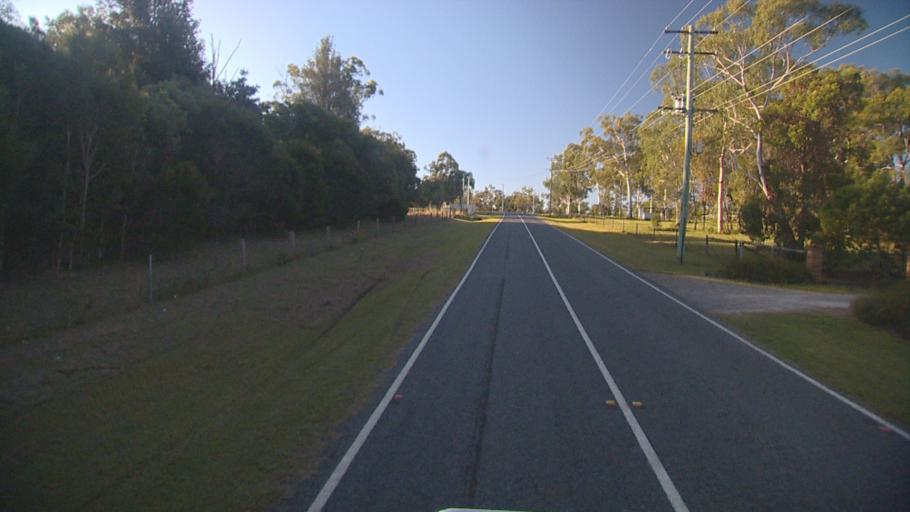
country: AU
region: Queensland
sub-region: Redland
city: Redland Bay
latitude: -27.6625
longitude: 153.2770
